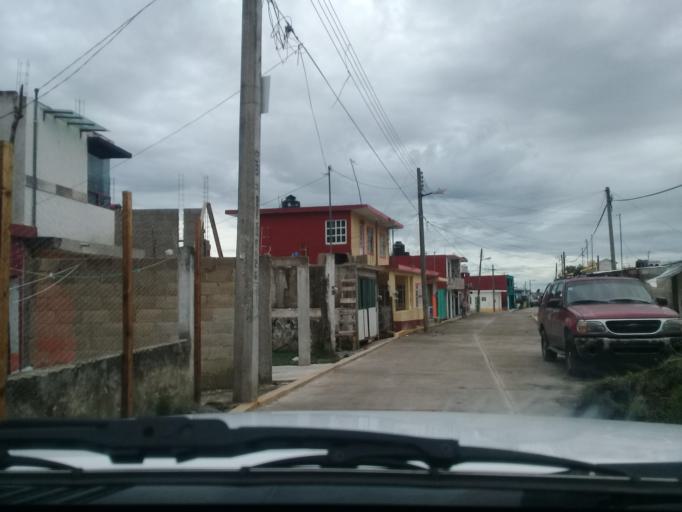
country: MX
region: Veracruz
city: Rafael Lucio
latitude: 19.5938
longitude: -96.9878
